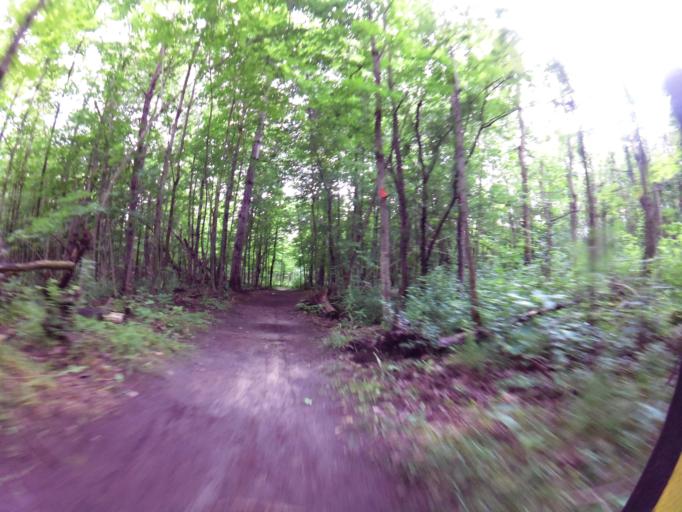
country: CA
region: Ontario
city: Bells Corners
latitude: 45.3005
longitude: -75.8451
